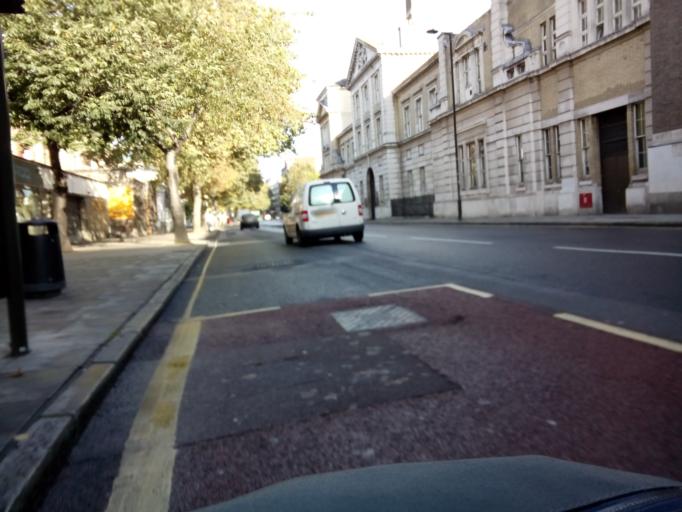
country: GB
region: England
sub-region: Greater London
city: Clerkenwell
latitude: 51.5256
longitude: -0.1175
